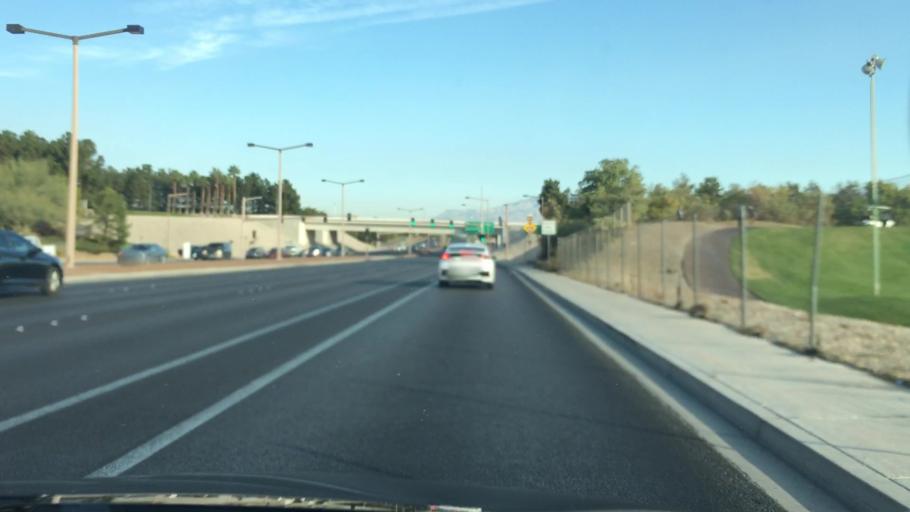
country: US
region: Nevada
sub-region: Clark County
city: Summerlin South
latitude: 36.1758
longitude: -115.2870
